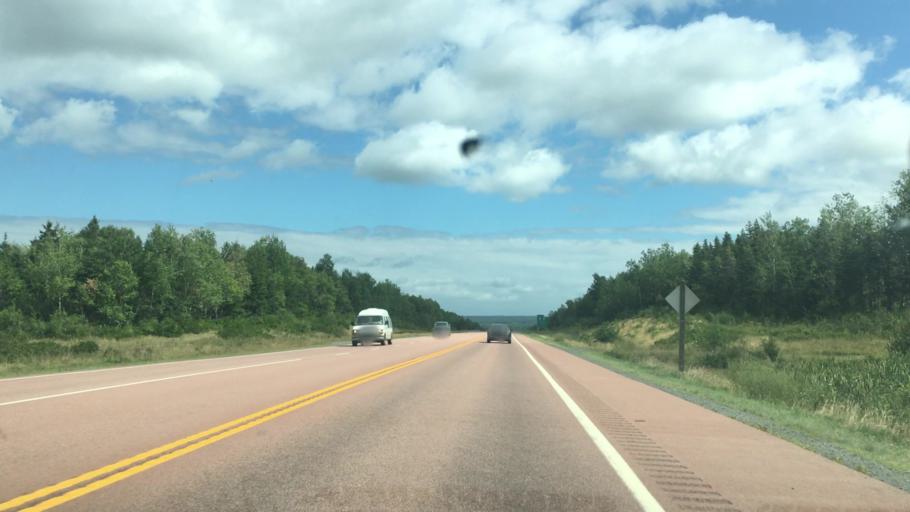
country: CA
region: Nova Scotia
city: Port Hawkesbury
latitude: 45.6095
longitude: -61.6522
